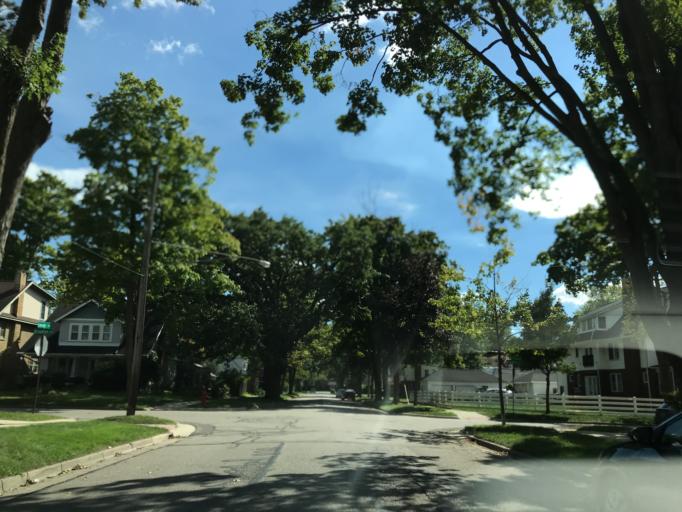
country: US
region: Michigan
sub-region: Washtenaw County
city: Ann Arbor
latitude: 42.2640
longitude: -83.7297
